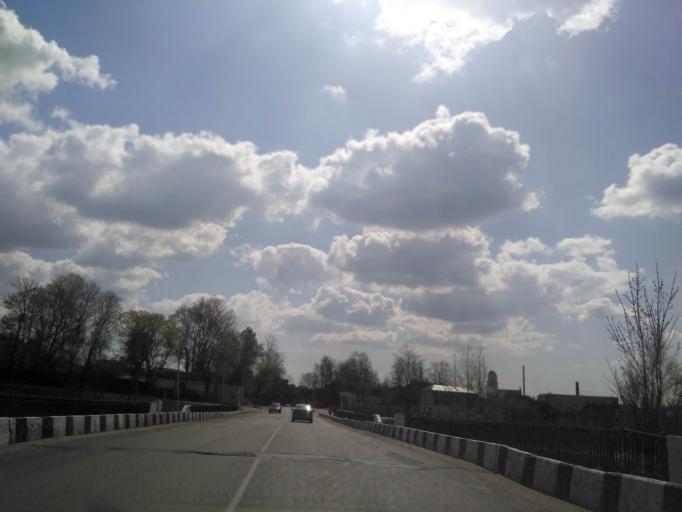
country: BY
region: Minsk
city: Radashkovichy
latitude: 54.1595
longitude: 27.2368
